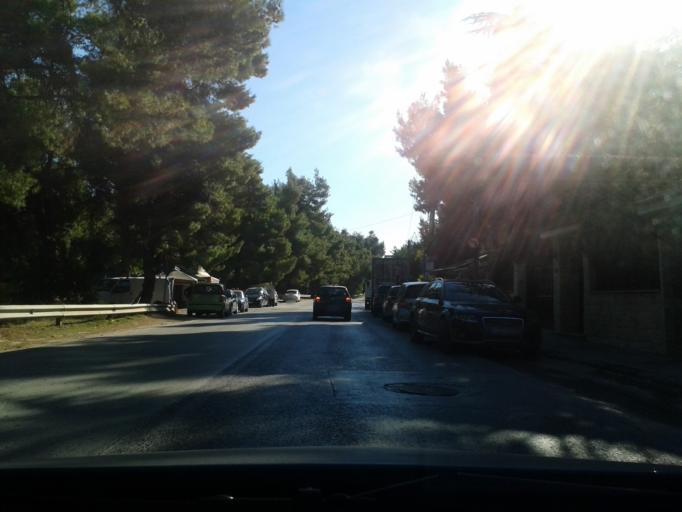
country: GR
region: Attica
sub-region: Nomarchia Anatolikis Attikis
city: Drosia
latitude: 38.1056
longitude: 23.8672
